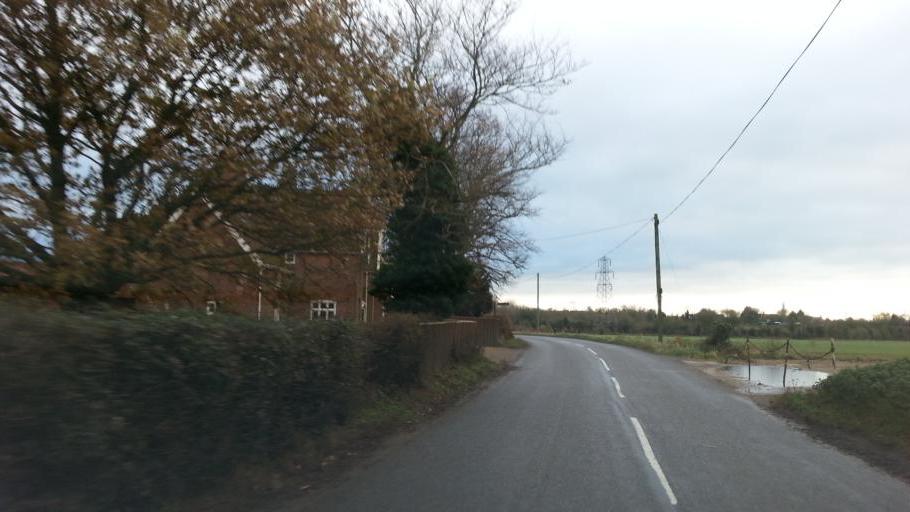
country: GB
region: England
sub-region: Suffolk
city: Framlingham
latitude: 52.3050
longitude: 1.3515
